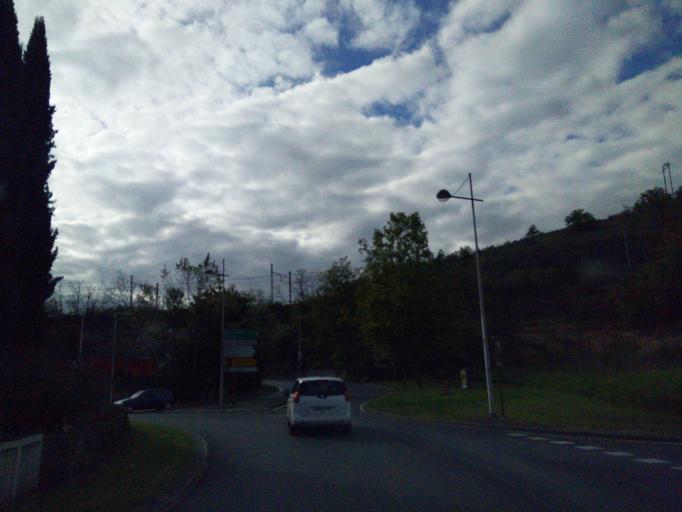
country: FR
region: Midi-Pyrenees
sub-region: Departement du Lot
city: Cahors
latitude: 44.4152
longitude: 1.4366
